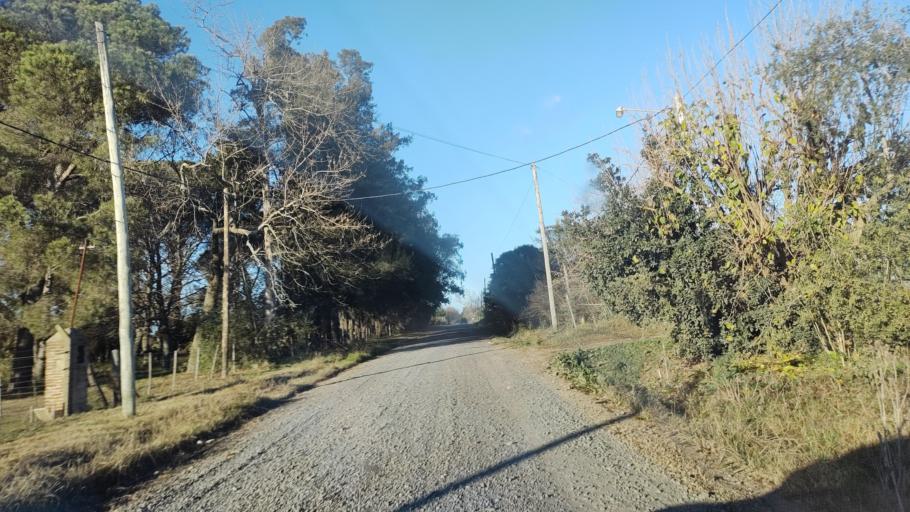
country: AR
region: Buenos Aires
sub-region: Partido de La Plata
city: La Plata
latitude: -34.9076
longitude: -58.0531
